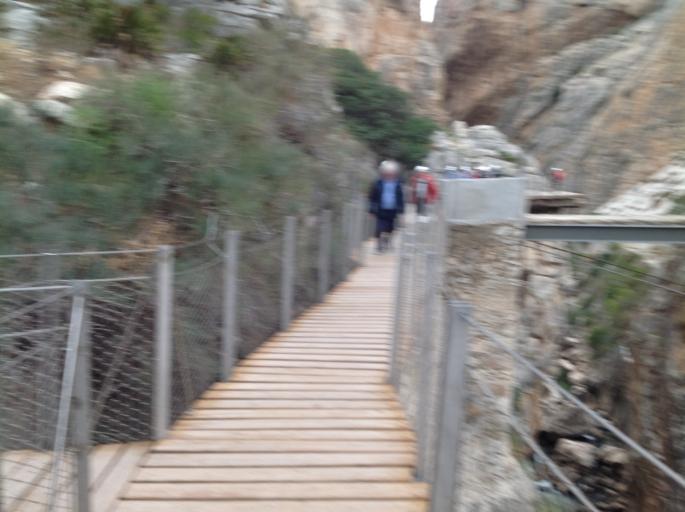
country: ES
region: Andalusia
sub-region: Provincia de Malaga
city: Ardales
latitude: 36.9283
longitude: -4.7825
